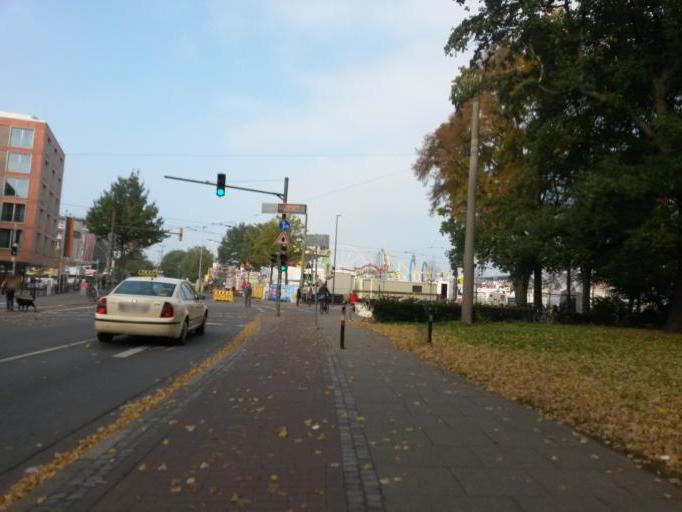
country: DE
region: Bremen
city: Bremen
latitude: 53.0839
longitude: 8.8170
